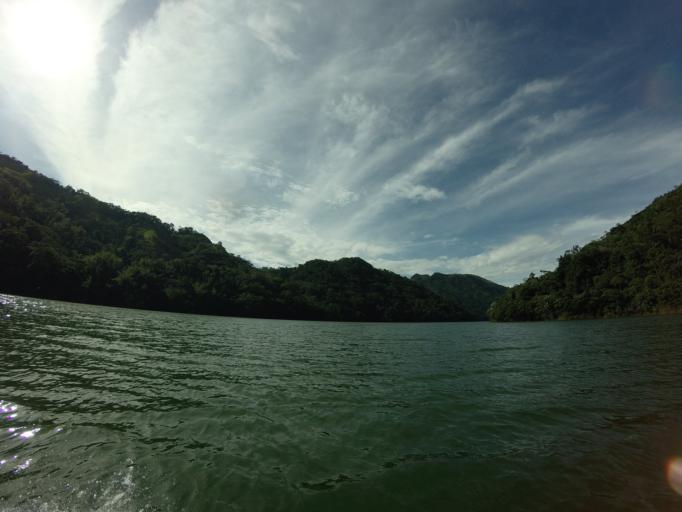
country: CO
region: Caldas
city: Norcasia
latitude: 5.5508
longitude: -74.9127
